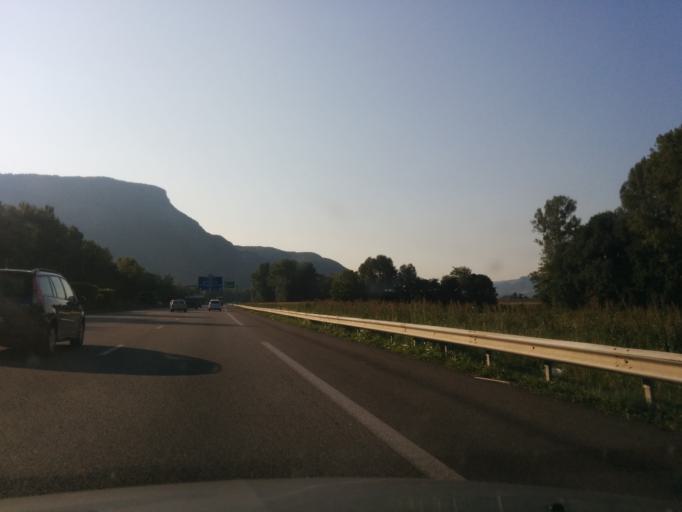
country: FR
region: Rhone-Alpes
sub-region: Departement de l'Isere
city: Noyarey
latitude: 45.2602
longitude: 5.6371
